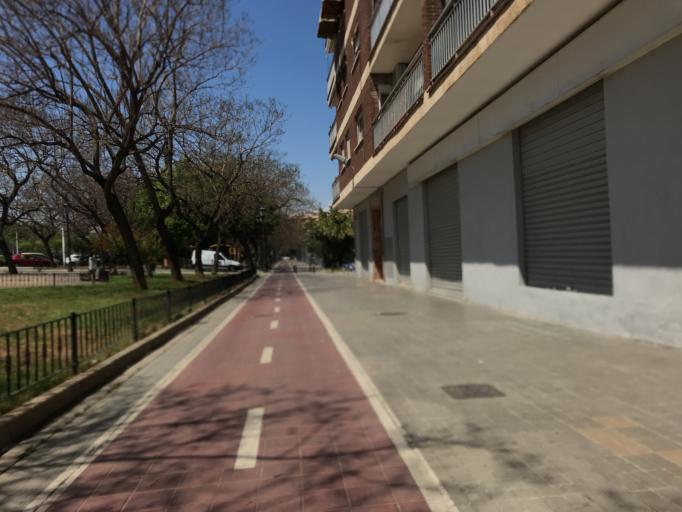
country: ES
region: Valencia
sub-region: Provincia de Valencia
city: Mislata
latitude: 39.4589
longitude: -0.4024
